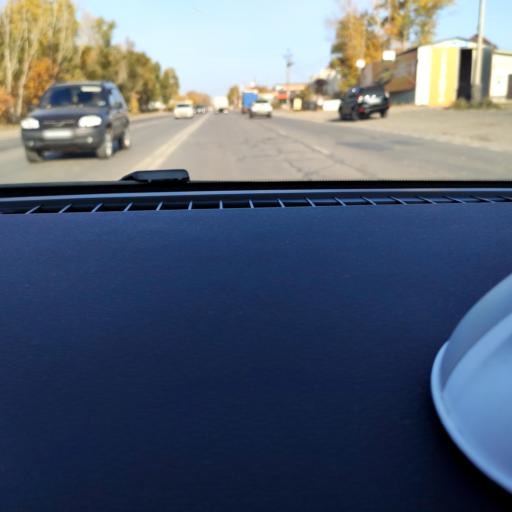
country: RU
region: Samara
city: Petra-Dubrava
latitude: 53.2629
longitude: 50.2879
